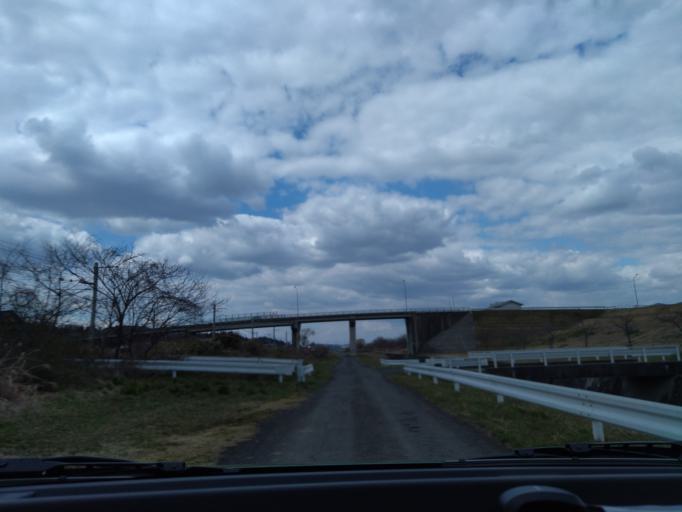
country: JP
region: Iwate
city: Ichinoseki
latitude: 38.9439
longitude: 141.1352
